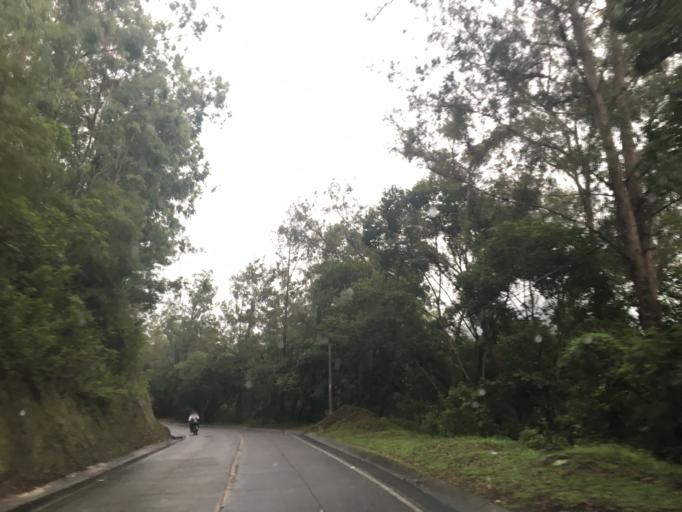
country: GT
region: Sacatepequez
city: Antigua Guatemala
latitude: 14.5663
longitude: -90.7279
